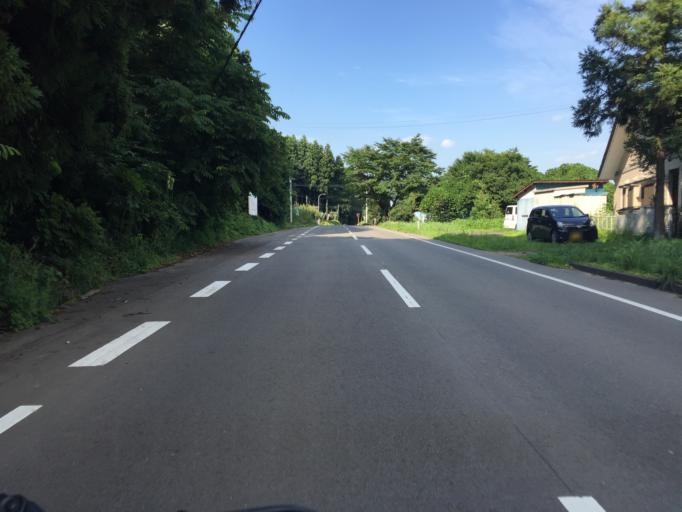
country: JP
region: Fukushima
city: Fukushima-shi
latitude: 37.7738
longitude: 140.3680
